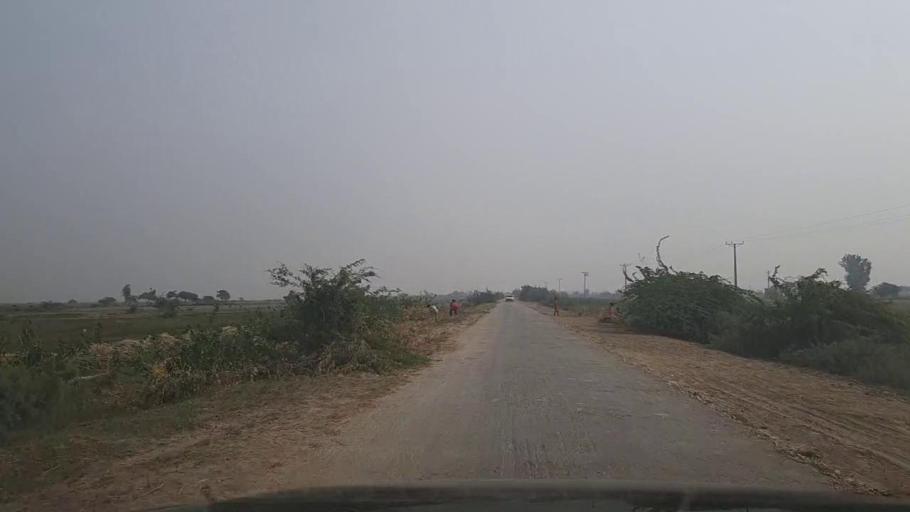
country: PK
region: Sindh
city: Mirpur Sakro
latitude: 24.4775
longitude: 67.6615
